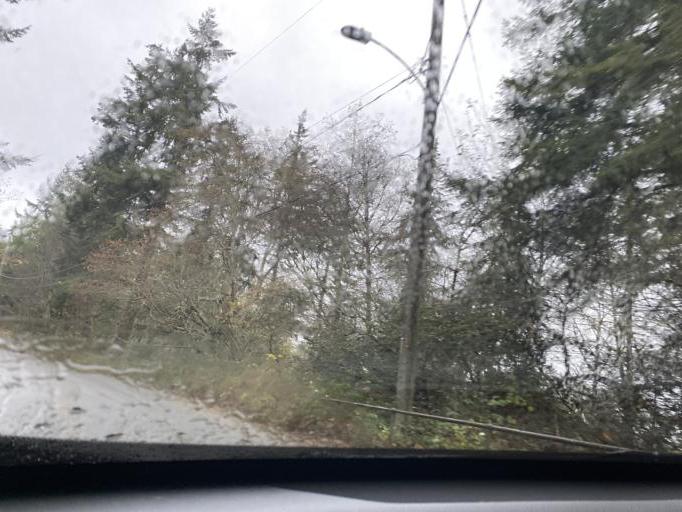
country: US
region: Washington
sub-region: King County
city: Seattle
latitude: 47.6619
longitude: -122.4115
